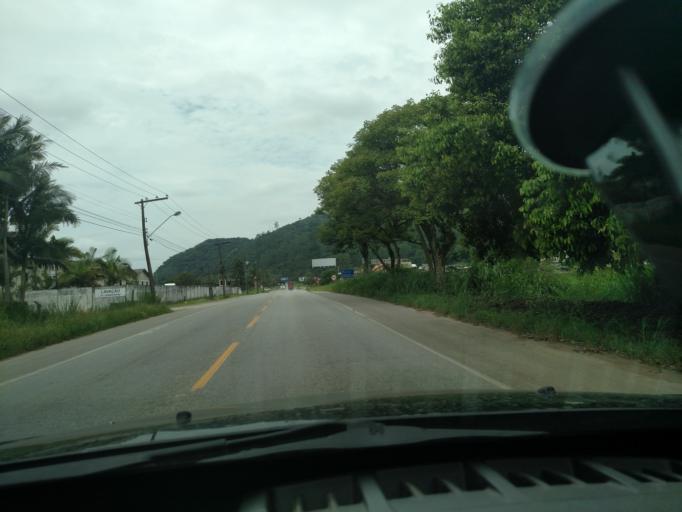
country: BR
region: Santa Catarina
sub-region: Itajai
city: Itajai
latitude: -26.8921
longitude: -48.7665
